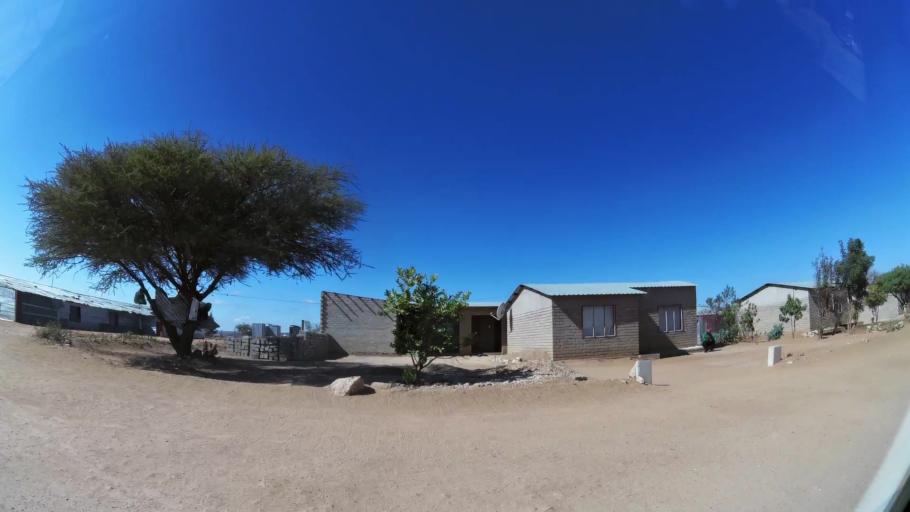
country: ZA
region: Limpopo
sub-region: Capricorn District Municipality
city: Polokwane
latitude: -23.8801
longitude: 29.4107
